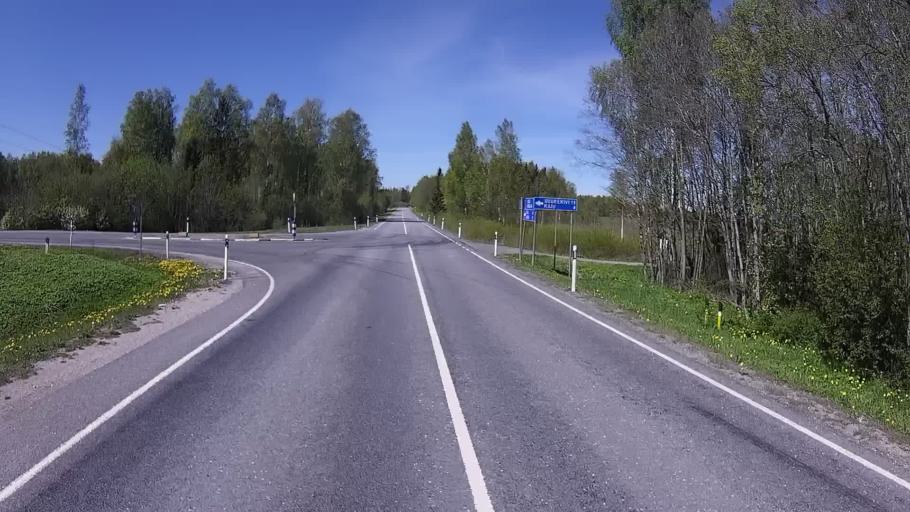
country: EE
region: Raplamaa
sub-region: Kehtna vald
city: Kehtna
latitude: 59.0428
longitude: 25.0314
